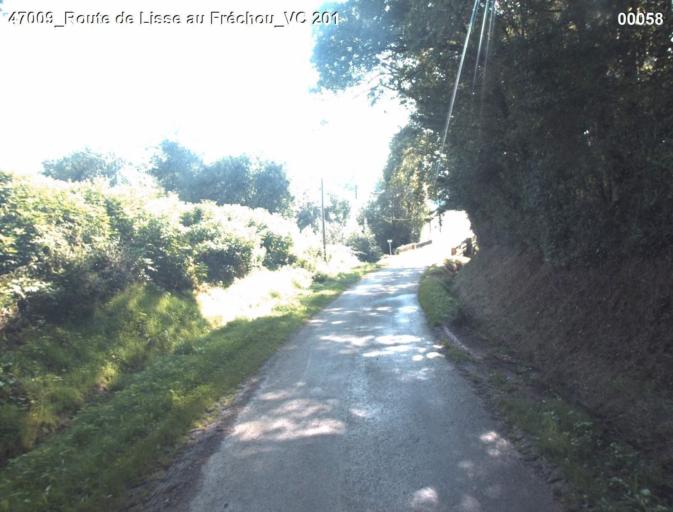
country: FR
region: Aquitaine
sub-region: Departement du Lot-et-Garonne
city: Nerac
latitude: 44.0934
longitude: 0.3100
